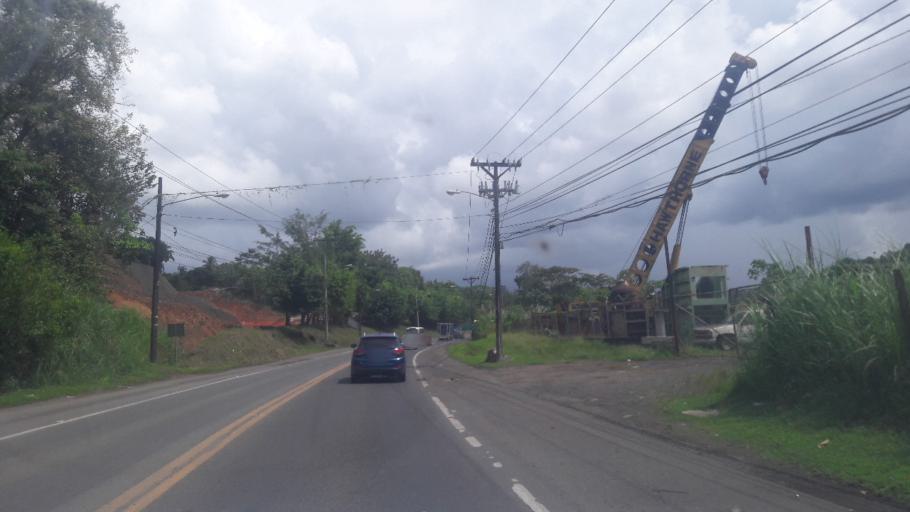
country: PA
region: Panama
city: Alcalde Diaz
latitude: 9.1271
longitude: -79.5835
